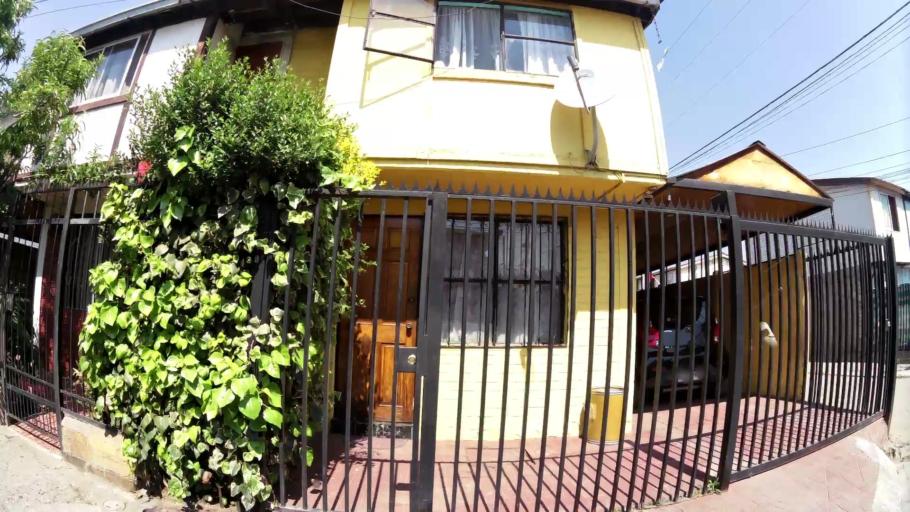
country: CL
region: Santiago Metropolitan
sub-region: Provincia de Santiago
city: La Pintana
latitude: -33.5531
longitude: -70.6145
